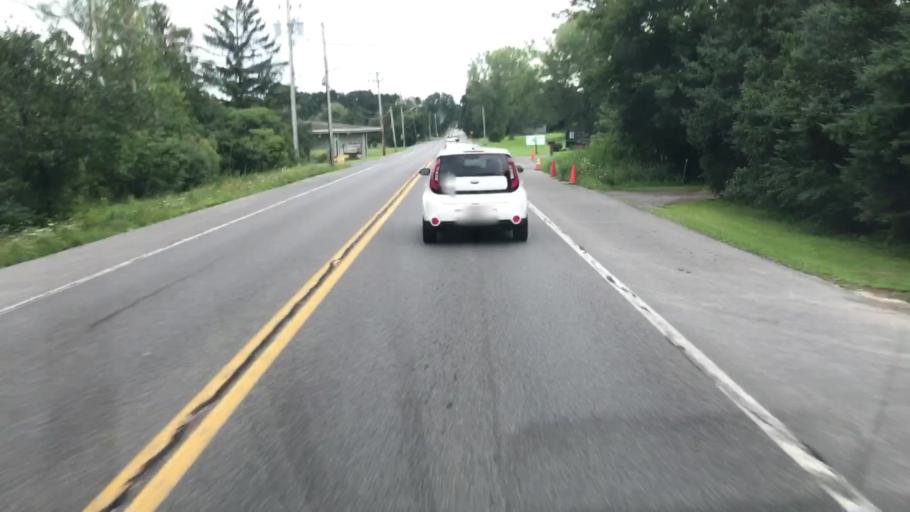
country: US
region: New York
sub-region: Onondaga County
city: North Syracuse
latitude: 43.1333
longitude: -76.1661
